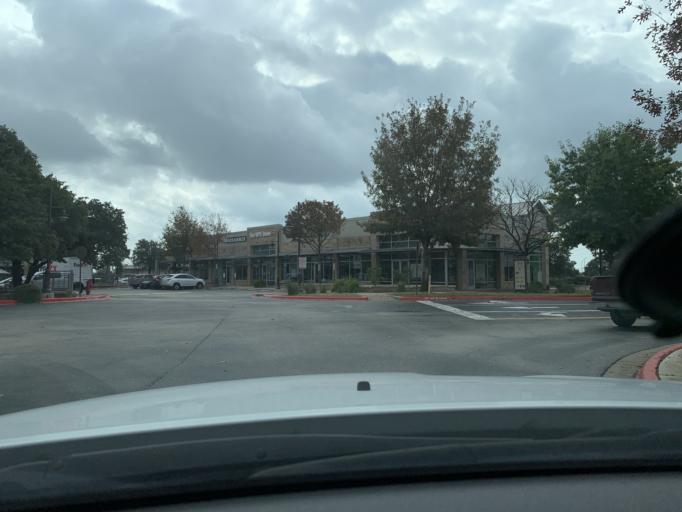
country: US
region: Texas
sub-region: Williamson County
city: Round Rock
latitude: 30.5608
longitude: -97.6909
